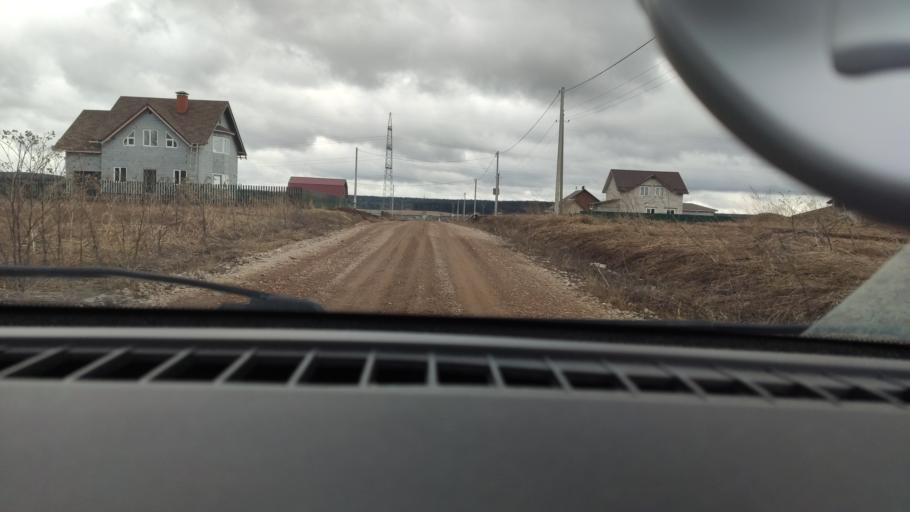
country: RU
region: Perm
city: Ferma
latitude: 57.9450
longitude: 56.3455
